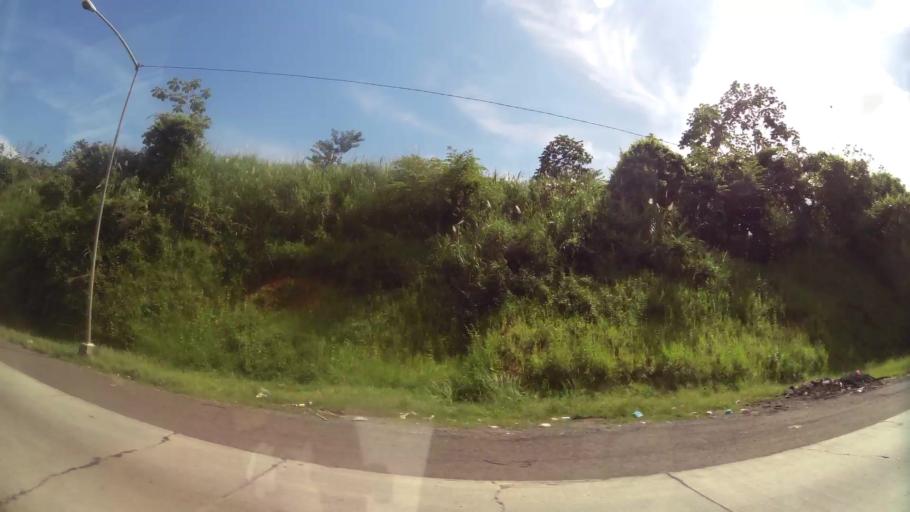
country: PA
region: Panama
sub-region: Distrito de Panama
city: Paraiso
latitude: 9.0370
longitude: -79.6252
